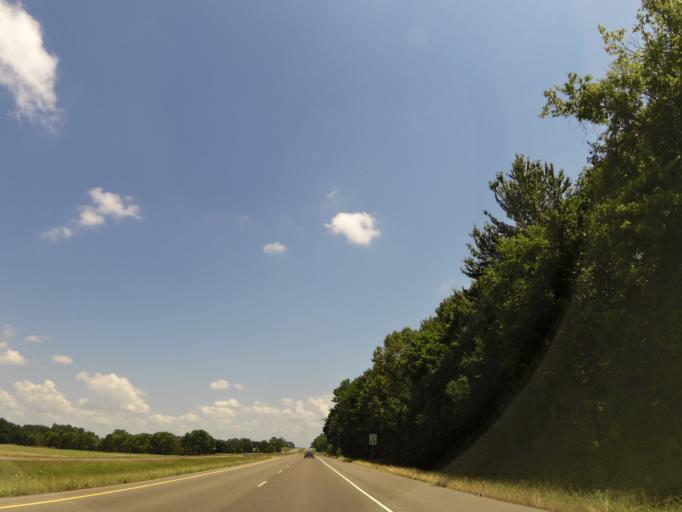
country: US
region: Tennessee
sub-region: Crockett County
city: Alamo
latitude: 35.8795
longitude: -89.2245
